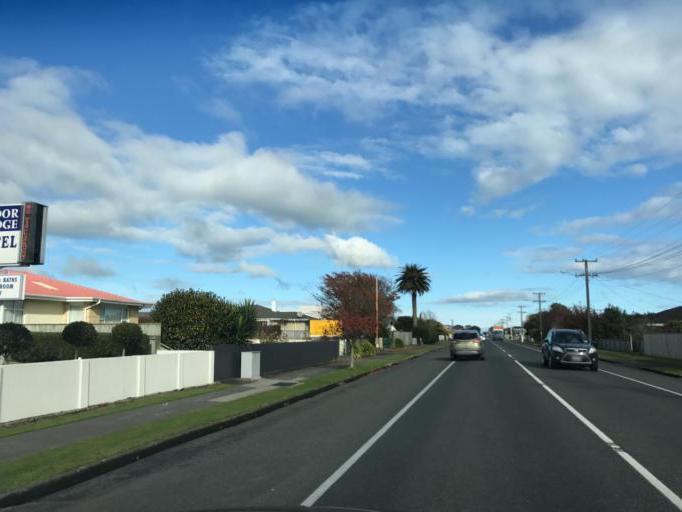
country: NZ
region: Taranaki
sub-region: South Taranaki District
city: Hawera
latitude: -39.5767
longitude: 174.2712
